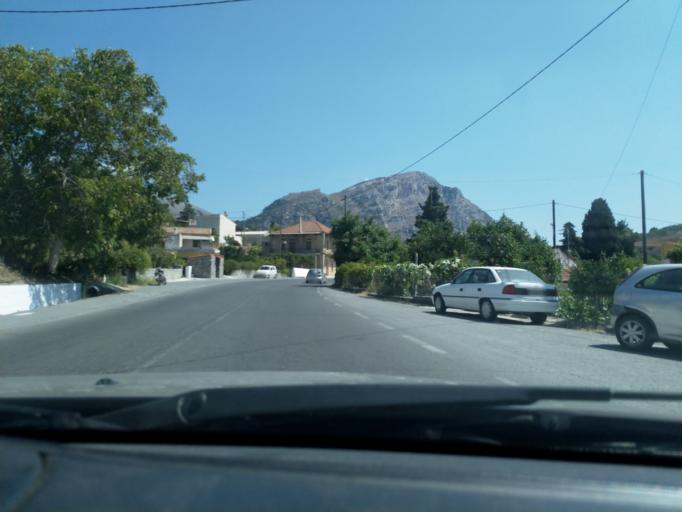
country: GR
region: Crete
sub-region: Nomos Rethymnis
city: Agia Foteini
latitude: 35.2205
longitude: 24.5191
